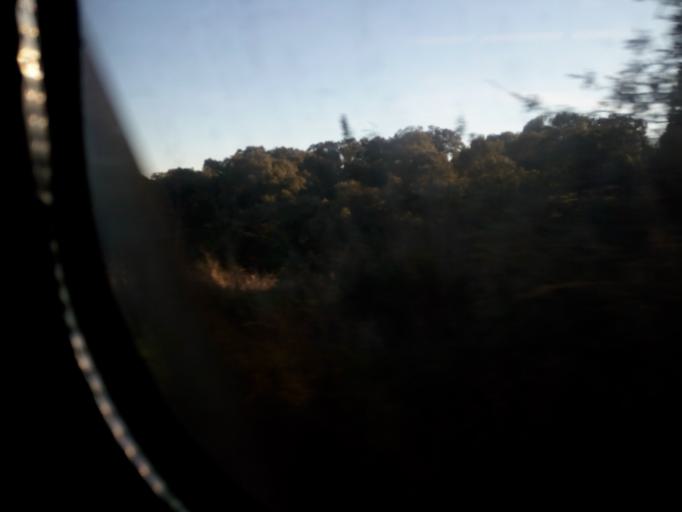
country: PT
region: Beja
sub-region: Odemira
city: Odemira
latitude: 37.6808
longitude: -8.4474
